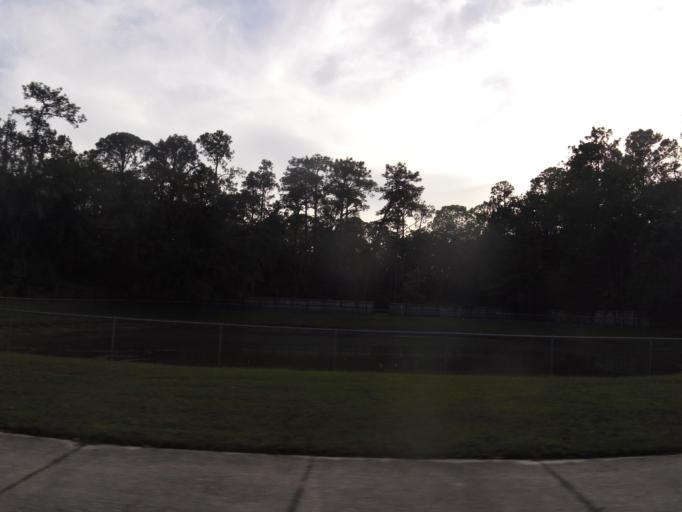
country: US
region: Florida
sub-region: Saint Johns County
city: Fruit Cove
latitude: 30.1601
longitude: -81.6240
